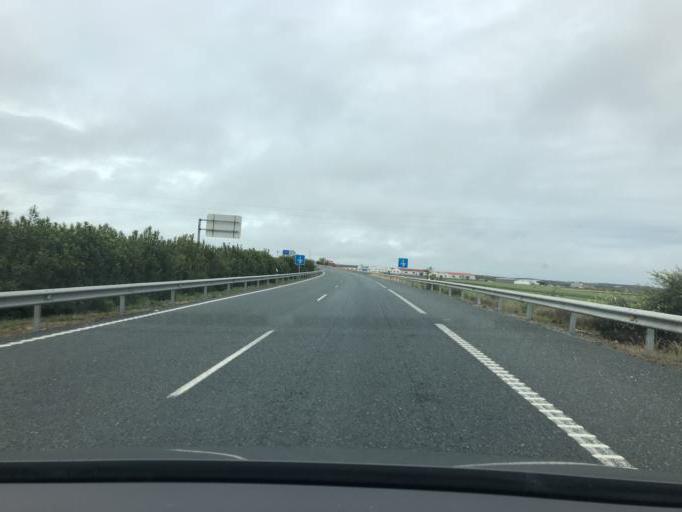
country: ES
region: Andalusia
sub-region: Provincia de Sevilla
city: El Arahal
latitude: 37.2529
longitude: -5.5428
